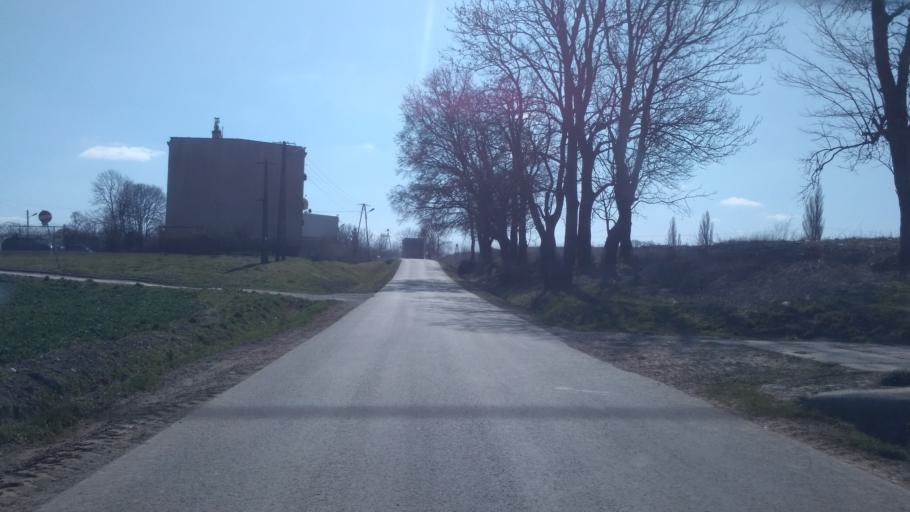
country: PL
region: Subcarpathian Voivodeship
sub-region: Powiat jaroslawski
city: Pawlosiow
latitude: 49.9560
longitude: 22.6498
